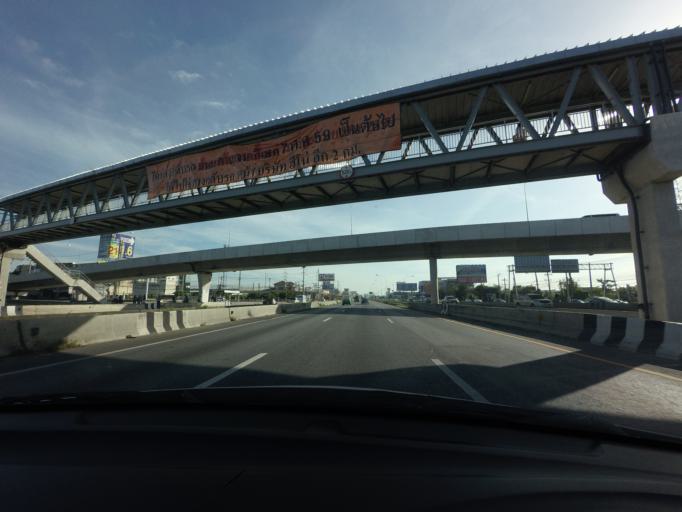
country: TH
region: Nonthaburi
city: Bang Bua Thong
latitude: 13.9251
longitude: 100.4132
